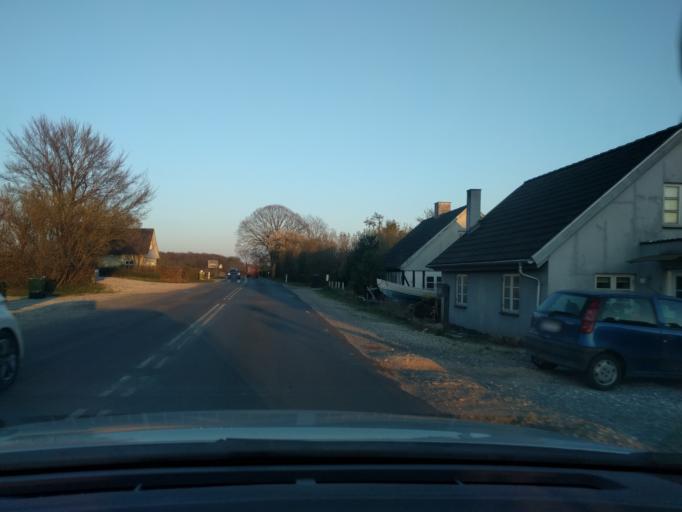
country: DK
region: South Denmark
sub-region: Assens Kommune
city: Glamsbjerg
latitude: 55.2692
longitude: 10.0754
